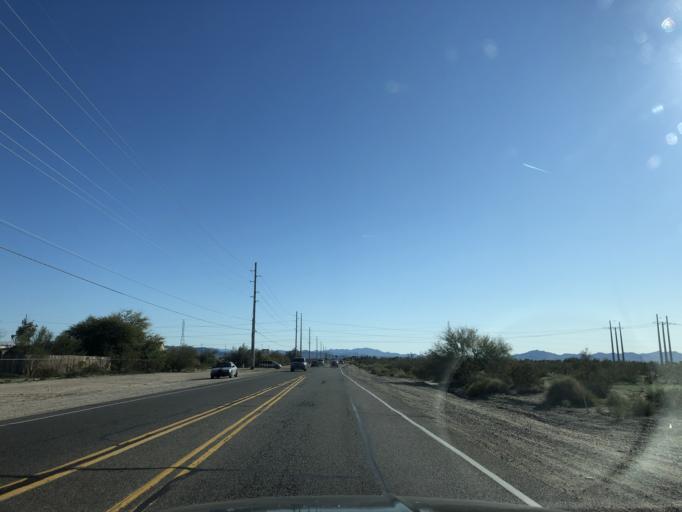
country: US
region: Arizona
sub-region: Maricopa County
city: Buckeye
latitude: 33.4257
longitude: -112.5908
